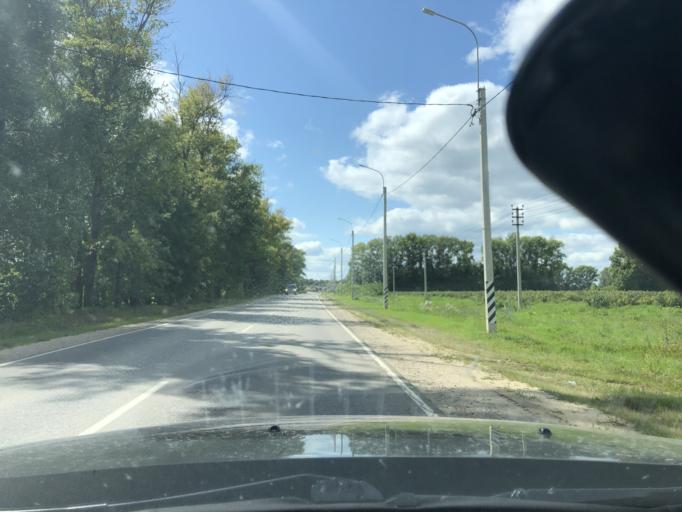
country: RU
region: Tula
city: Gorelki
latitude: 54.3413
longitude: 37.5716
